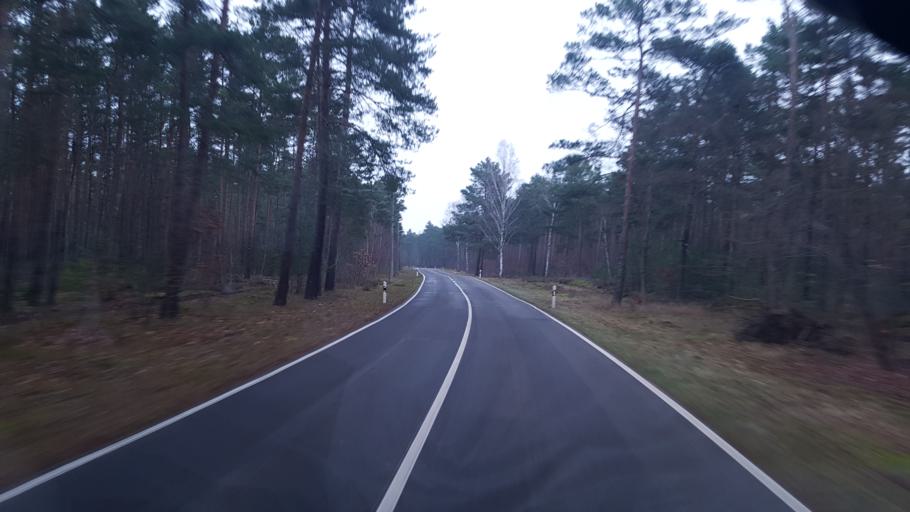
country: DE
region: Brandenburg
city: Drachhausen
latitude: 51.8816
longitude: 14.2983
